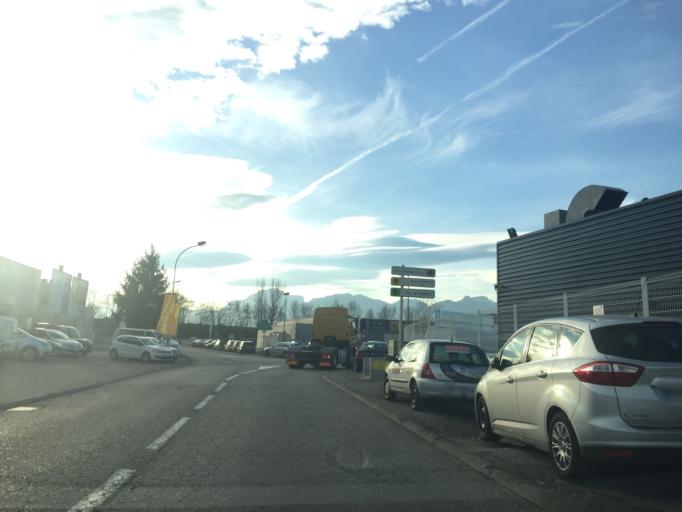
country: FR
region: Rhone-Alpes
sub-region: Departement de la Savoie
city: La Motte-Servolex
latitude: 45.6097
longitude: 5.8892
